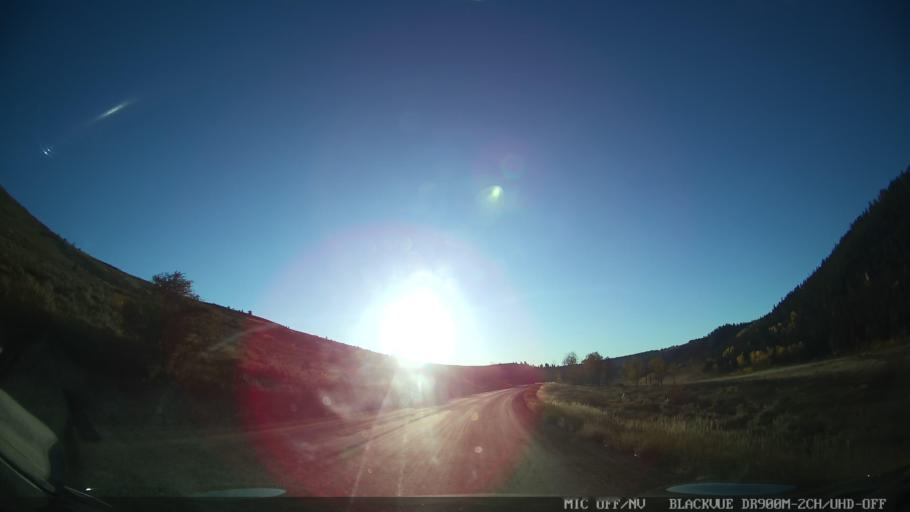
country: US
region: Colorado
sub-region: Grand County
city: Kremmling
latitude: 39.9921
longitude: -106.4510
